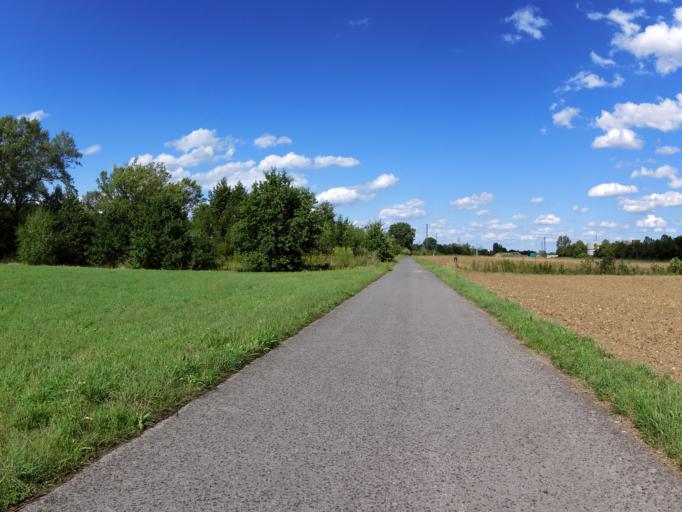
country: DE
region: Bavaria
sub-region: Regierungsbezirk Unterfranken
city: Sulzfeld am Main
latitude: 49.7084
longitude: 10.1382
